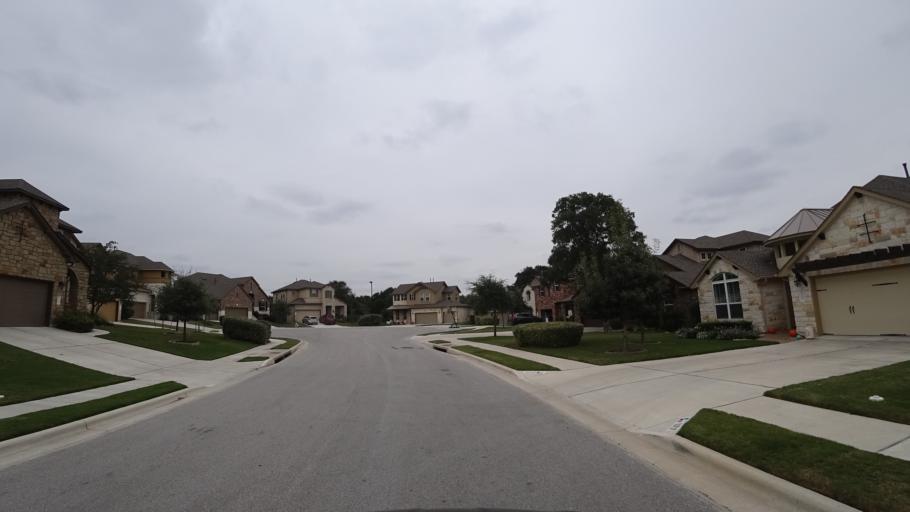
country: US
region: Texas
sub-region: Travis County
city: Shady Hollow
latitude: 30.1823
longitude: -97.9060
